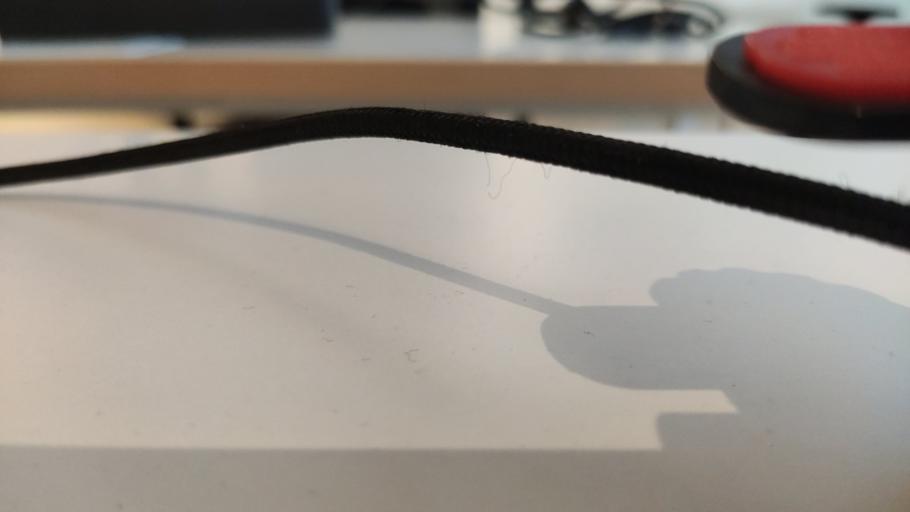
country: RU
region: Moskovskaya
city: Novopetrovskoye
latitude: 55.9094
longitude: 36.4427
